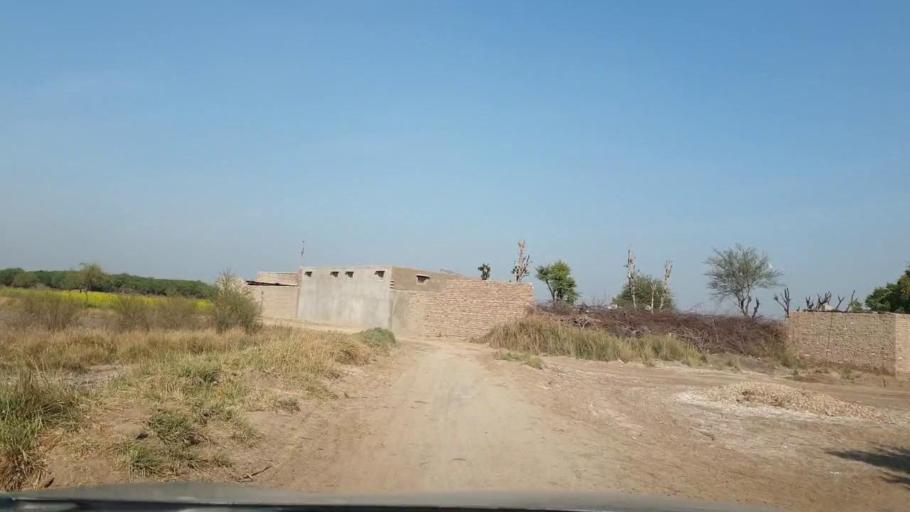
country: PK
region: Sindh
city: Berani
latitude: 25.7181
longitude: 68.7743
